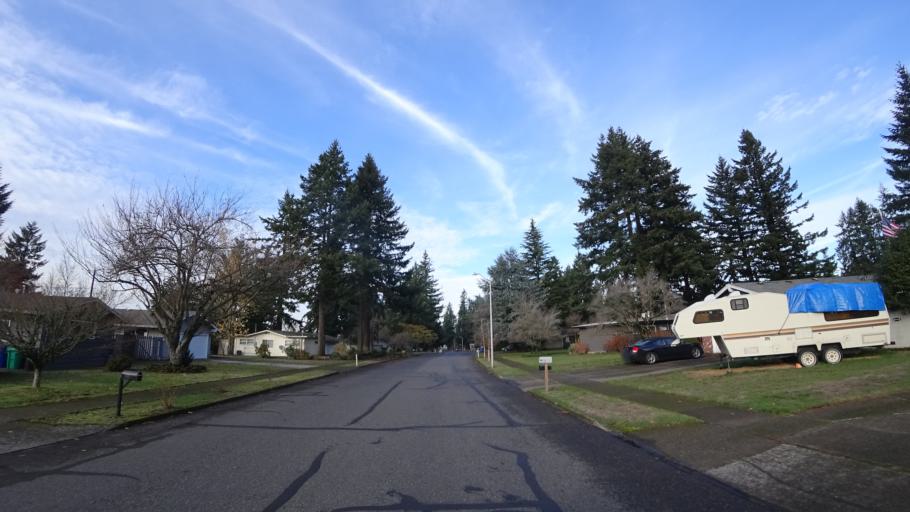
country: US
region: Oregon
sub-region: Multnomah County
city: Lents
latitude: 45.5278
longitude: -122.5280
